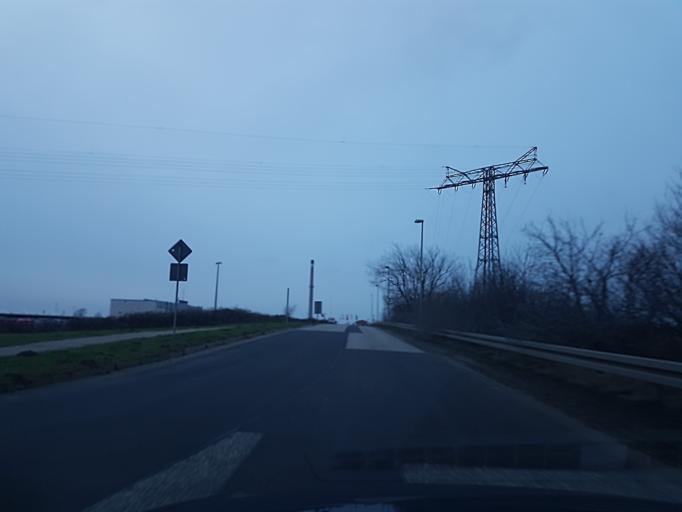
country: DE
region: Mecklenburg-Vorpommern
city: Sagard
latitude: 54.4907
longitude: 13.5835
